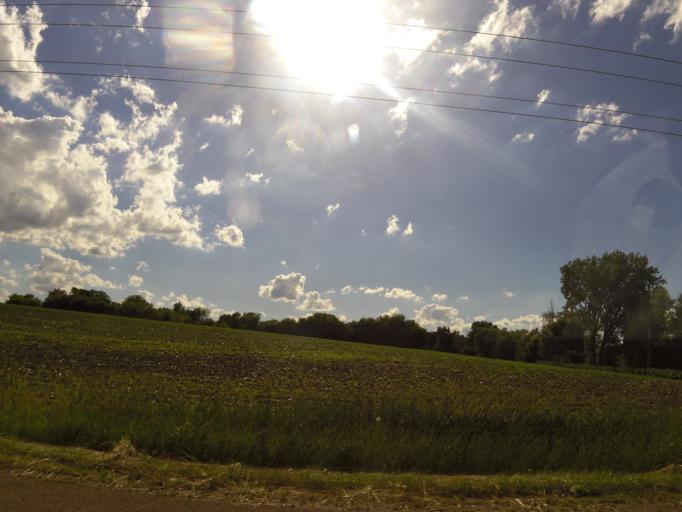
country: US
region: Minnesota
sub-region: Carver County
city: Waconia
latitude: 44.8528
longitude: -93.8192
